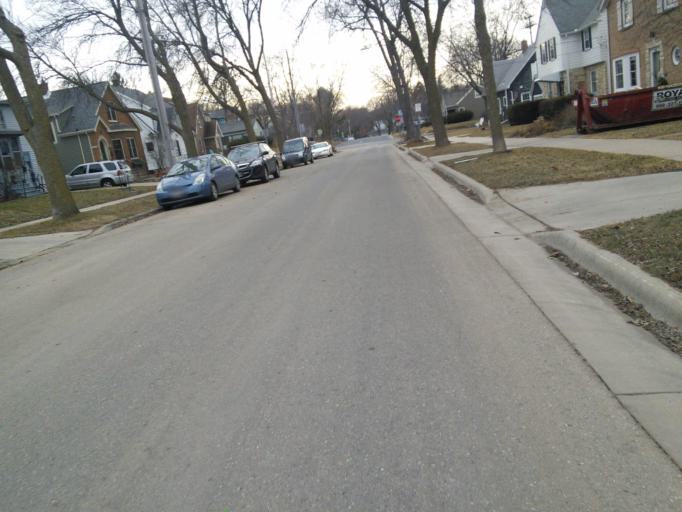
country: US
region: Wisconsin
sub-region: Dane County
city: Shorewood Hills
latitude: 43.0715
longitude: -89.4353
